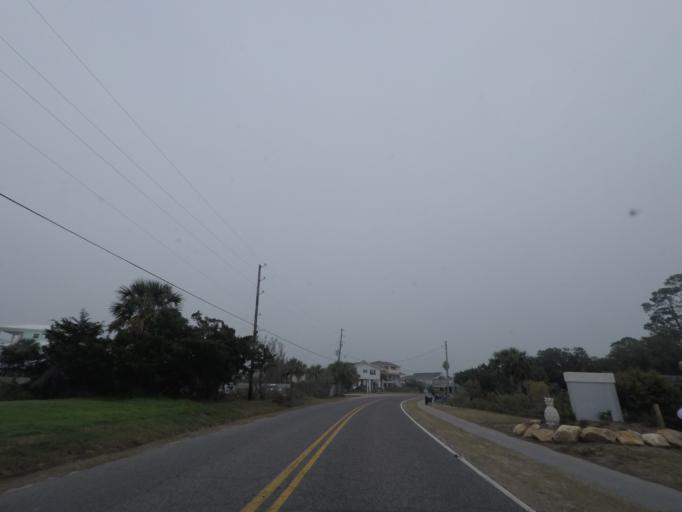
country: US
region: South Carolina
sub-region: Charleston County
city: Seabrook Island
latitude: 32.4919
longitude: -80.3283
